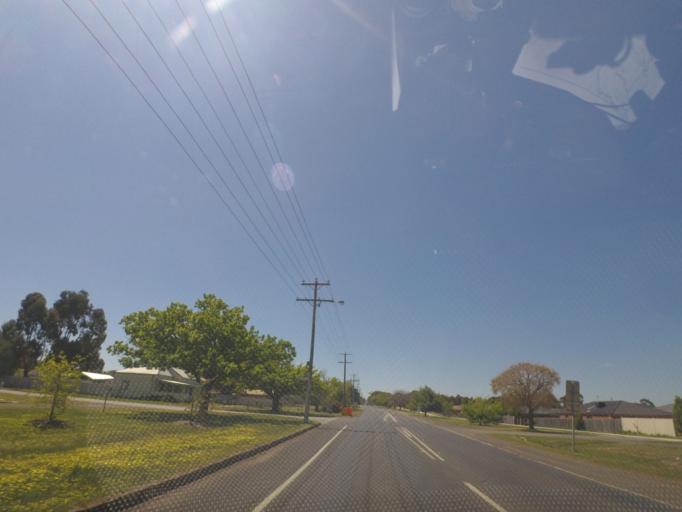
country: AU
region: Victoria
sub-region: Hume
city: Sunbury
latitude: -37.4591
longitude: 144.6812
